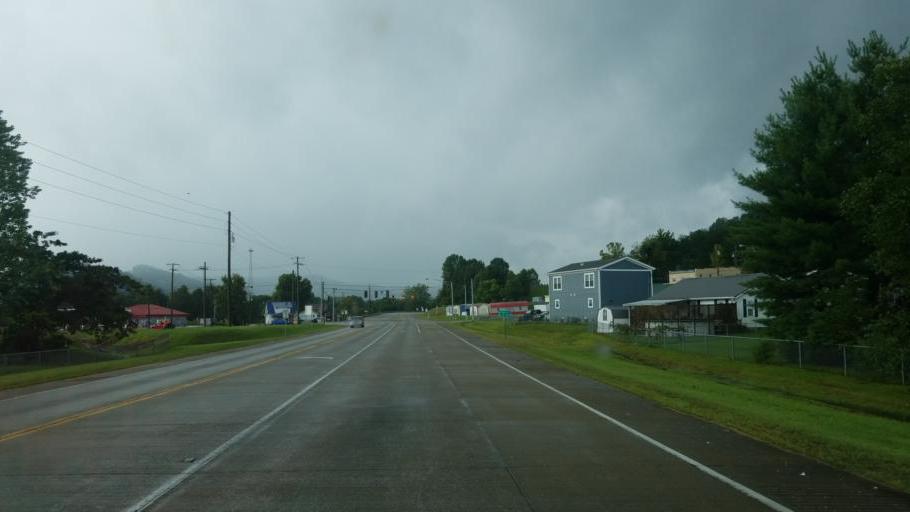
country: US
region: Kentucky
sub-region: Rowan County
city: Morehead
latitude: 38.1712
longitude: -83.4387
